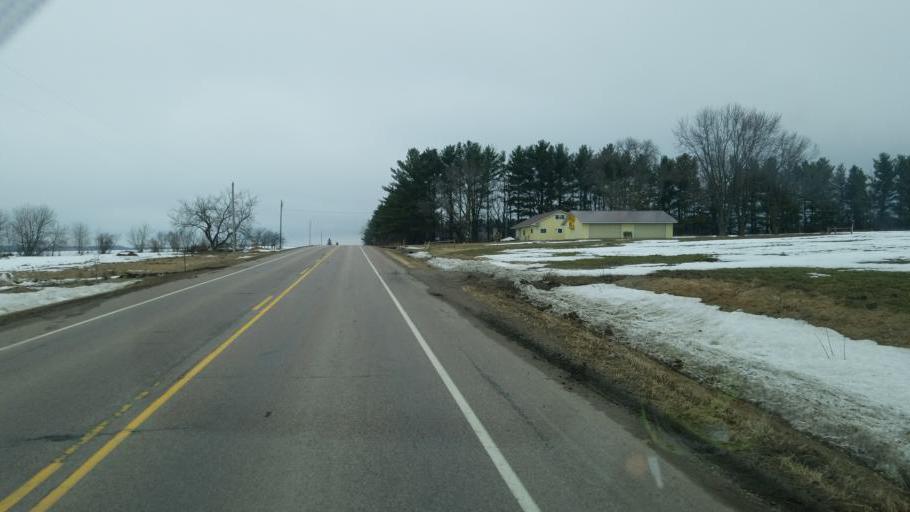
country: US
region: Wisconsin
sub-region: Wood County
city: Marshfield
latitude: 44.6475
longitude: -90.2184
